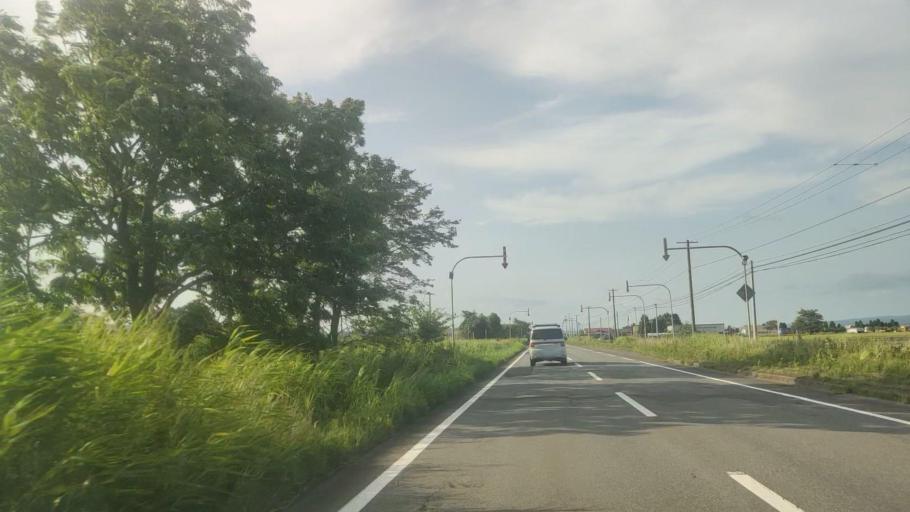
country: JP
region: Hokkaido
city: Chitose
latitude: 42.9562
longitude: 141.7987
